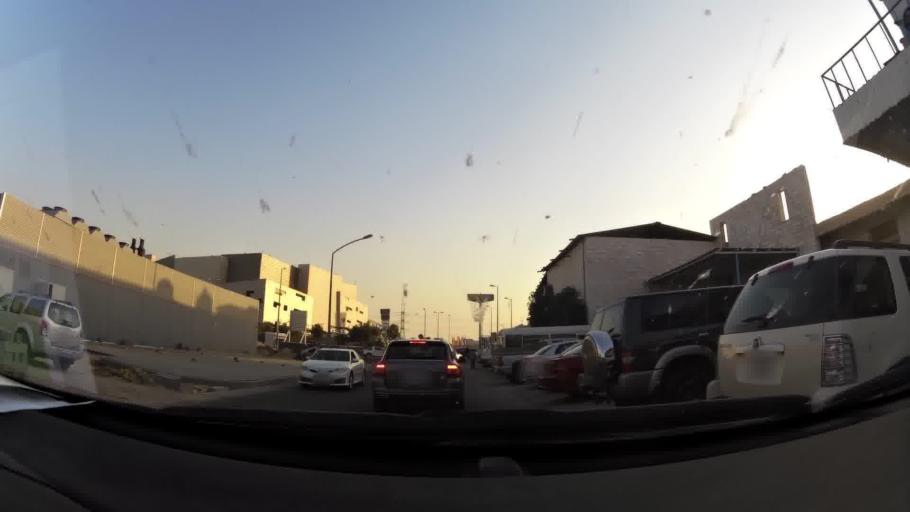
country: KW
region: Al Asimah
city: Ar Rabiyah
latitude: 29.3040
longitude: 47.9287
